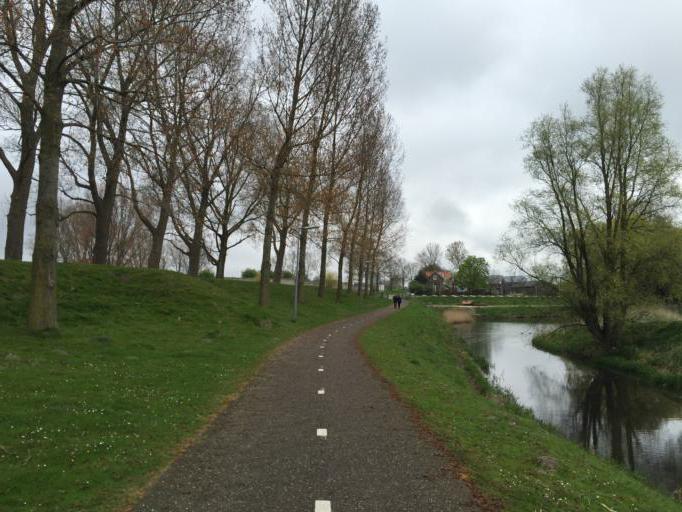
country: NL
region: North Holland
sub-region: Gemeente Haarlemmermeer
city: Hoofddorp
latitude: 52.3451
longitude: 4.6722
